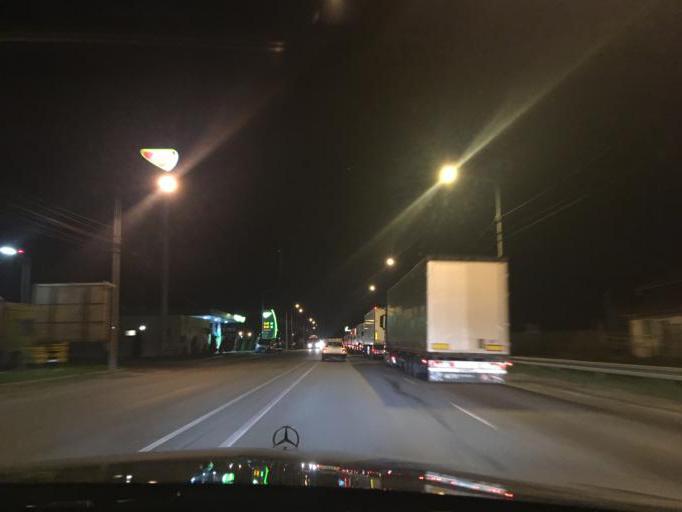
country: RO
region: Bihor
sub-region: Comuna Bors
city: Bors
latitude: 47.1149
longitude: 21.8067
